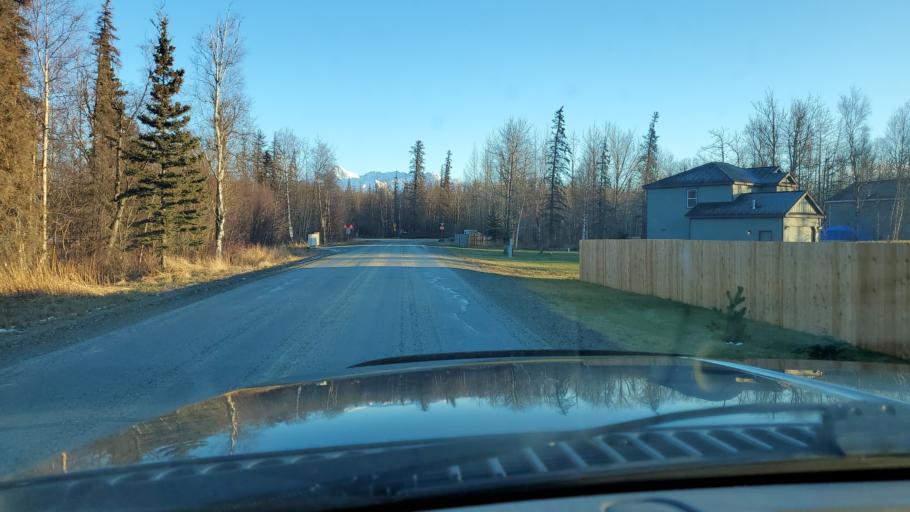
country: US
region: Alaska
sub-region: Matanuska-Susitna Borough
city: Gateway
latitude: 61.5885
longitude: -149.2493
